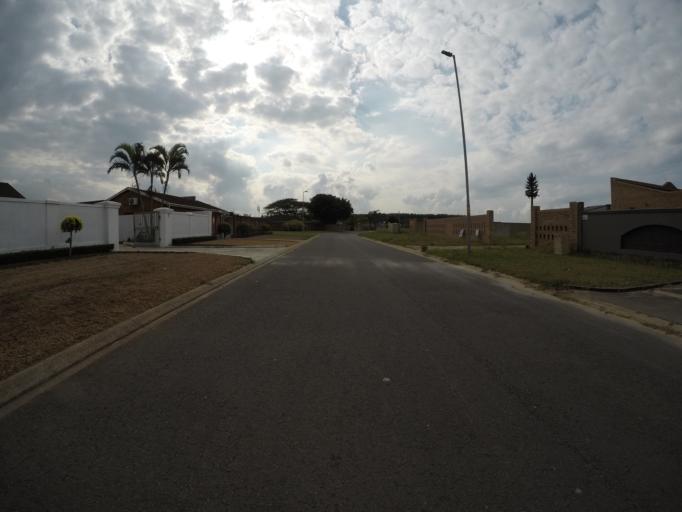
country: ZA
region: KwaZulu-Natal
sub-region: uThungulu District Municipality
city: Richards Bay
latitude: -28.7348
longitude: 32.0861
